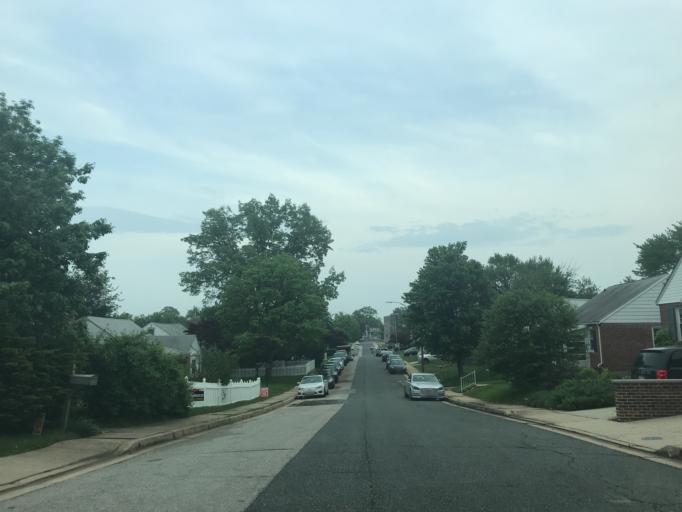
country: US
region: Maryland
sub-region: Baltimore County
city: Parkville
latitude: 39.3874
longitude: -76.5357
